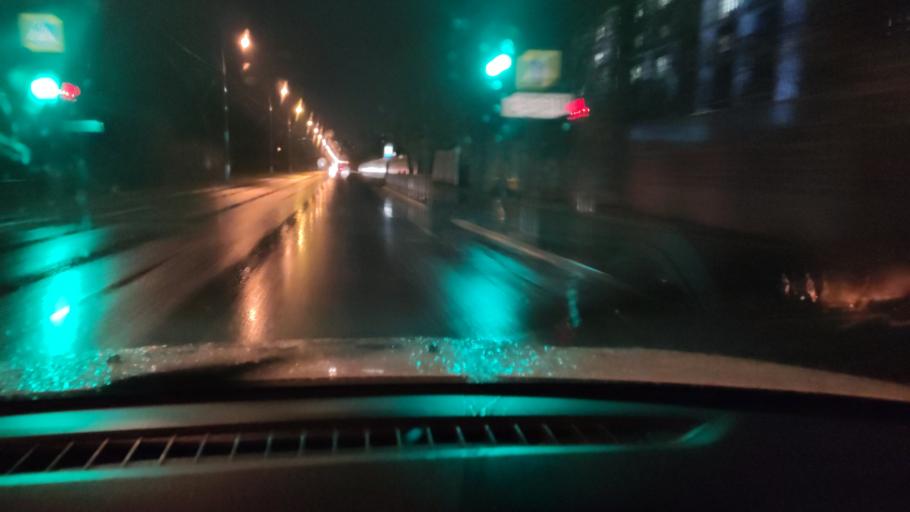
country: RU
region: Perm
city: Kondratovo
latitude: 57.9771
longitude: 56.1298
